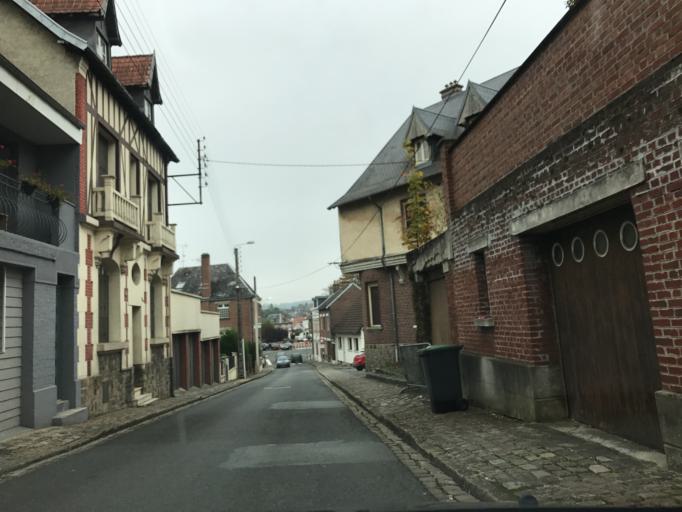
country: FR
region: Picardie
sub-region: Departement de la Somme
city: Peronne
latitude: 49.9277
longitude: 2.9320
